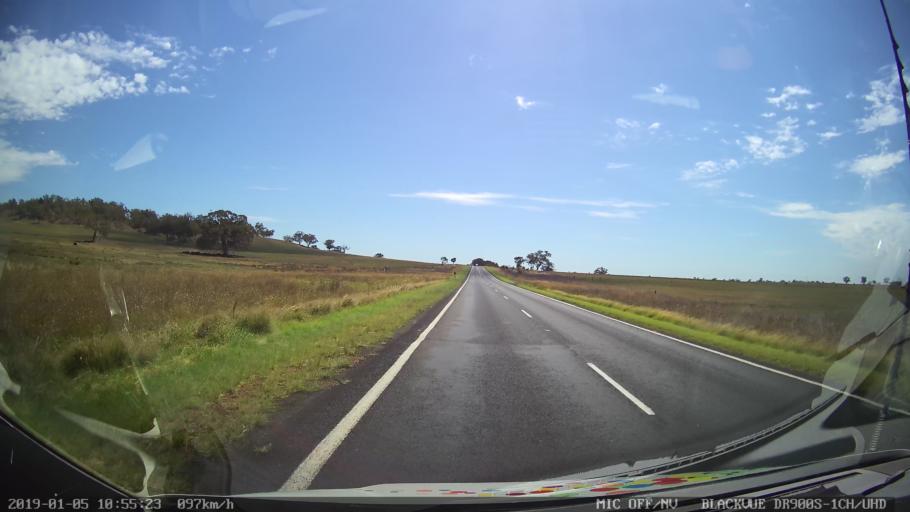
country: AU
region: New South Wales
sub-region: Warrumbungle Shire
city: Coonabarabran
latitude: -31.4486
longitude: 149.1429
